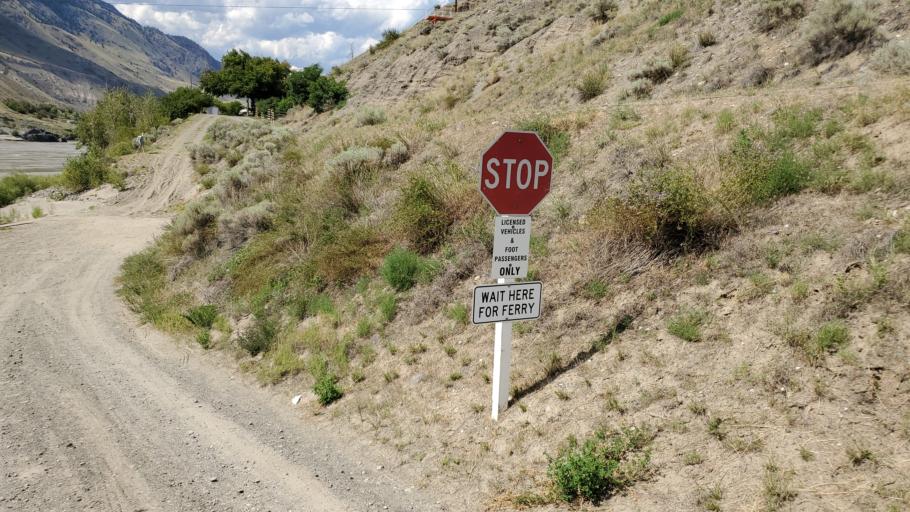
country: CA
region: British Columbia
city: Lillooet
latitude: 51.1834
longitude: -122.1306
